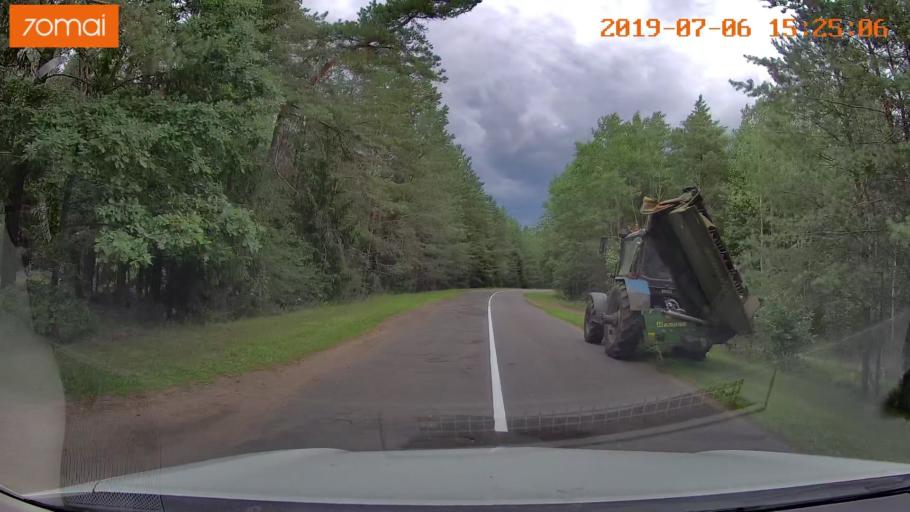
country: BY
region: Minsk
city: Valozhyn
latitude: 54.0277
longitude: 26.6036
